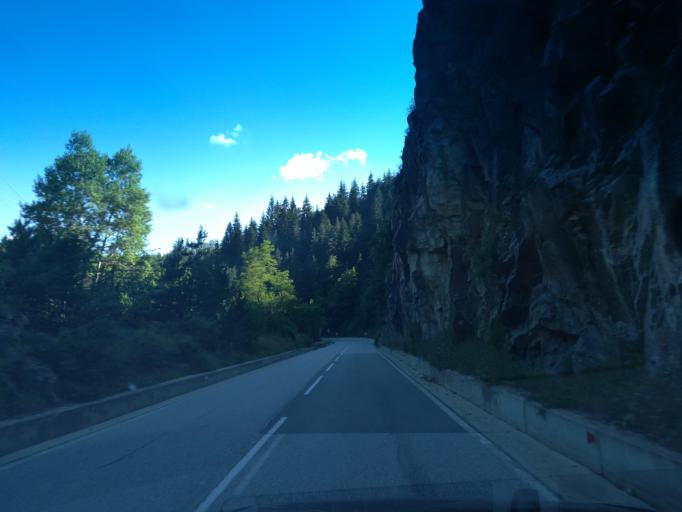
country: BG
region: Smolyan
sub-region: Obshtina Chepelare
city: Chepelare
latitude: 41.7780
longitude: 24.7075
